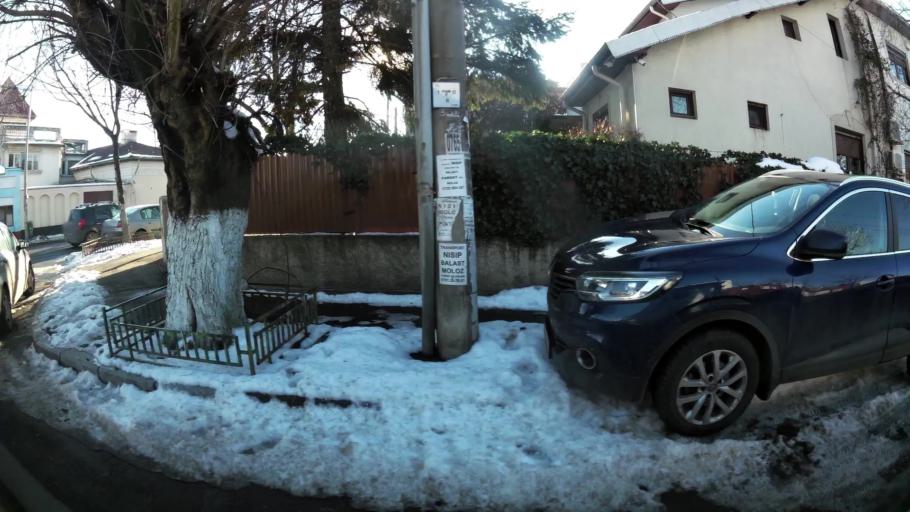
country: RO
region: Bucuresti
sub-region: Municipiul Bucuresti
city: Bucuresti
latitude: 44.4019
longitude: 26.0912
